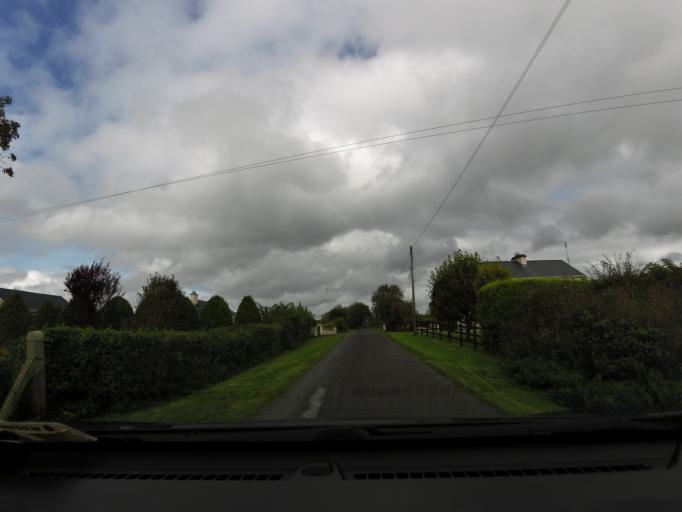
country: IE
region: Connaught
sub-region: County Galway
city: Athenry
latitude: 53.2892
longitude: -8.6644
